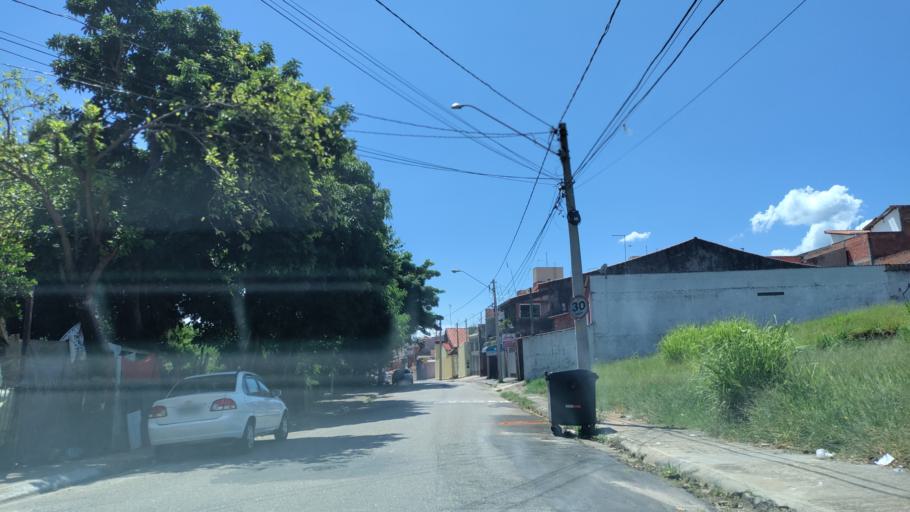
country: BR
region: Sao Paulo
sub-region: Sorocaba
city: Sorocaba
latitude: -23.4697
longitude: -47.4799
